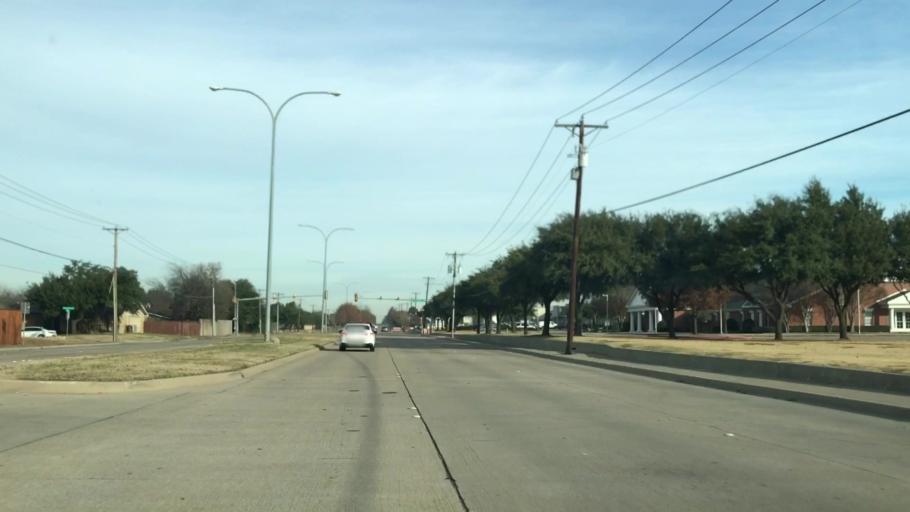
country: US
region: Texas
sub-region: Tarrant County
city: Watauga
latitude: 32.8764
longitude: -97.2896
